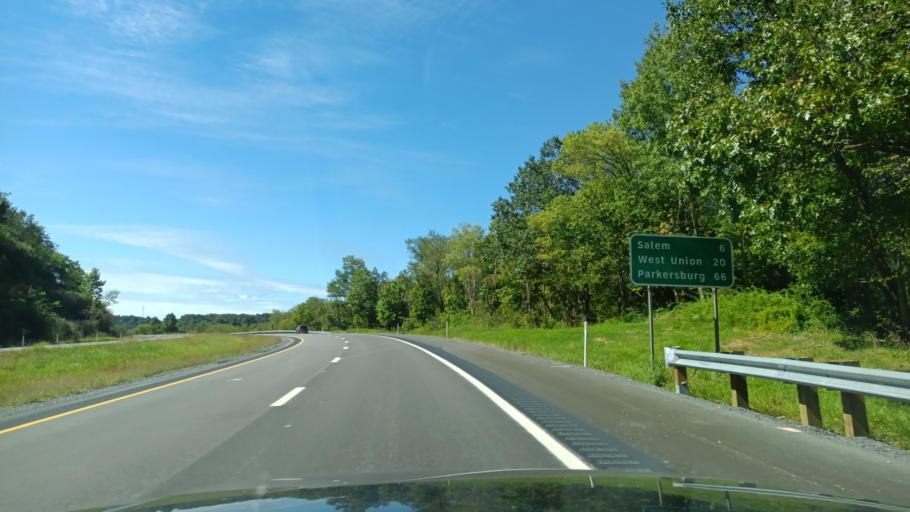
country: US
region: West Virginia
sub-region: Harrison County
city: Salem
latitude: 39.2820
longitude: -80.4534
